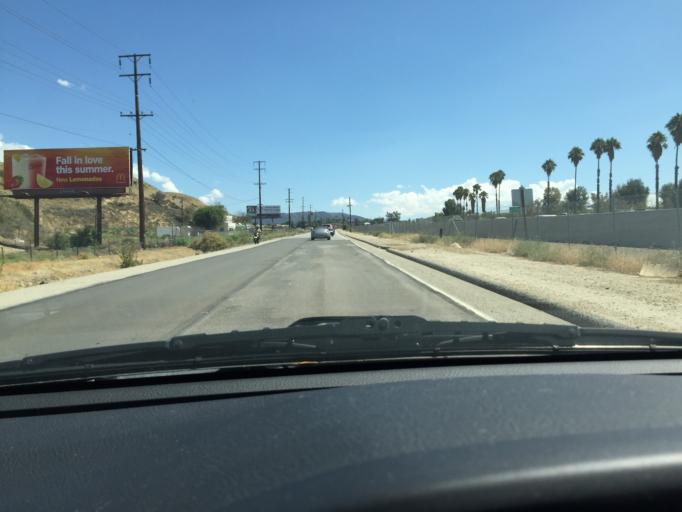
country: US
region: California
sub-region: Riverside County
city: Calimesa
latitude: 34.0140
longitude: -117.0795
